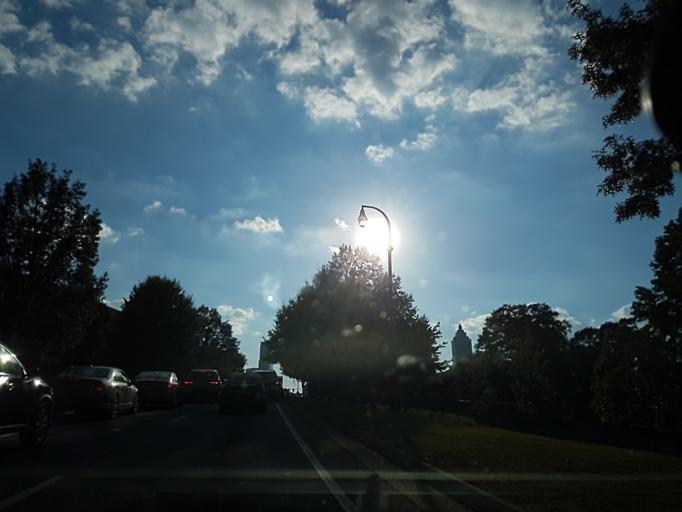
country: US
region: Georgia
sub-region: Fulton County
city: Atlanta
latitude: 33.7605
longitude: -84.3697
